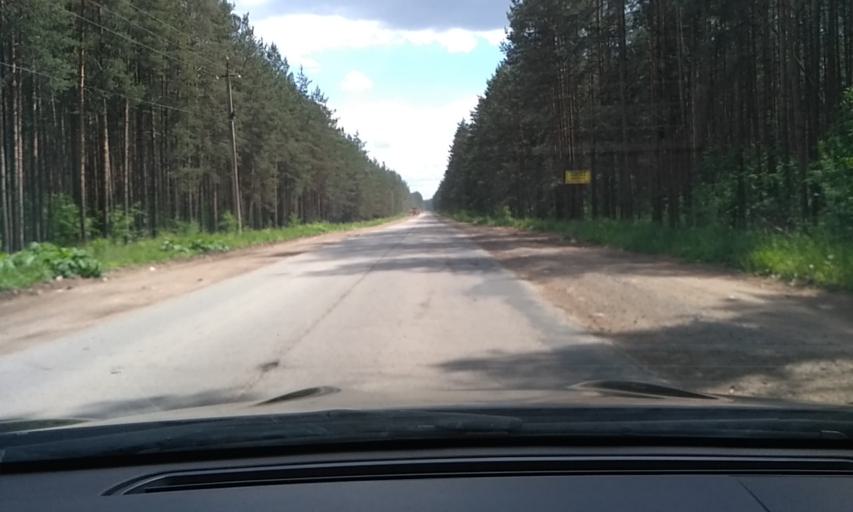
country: RU
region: Leningrad
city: Imeni Sverdlova
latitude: 59.8536
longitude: 30.6764
